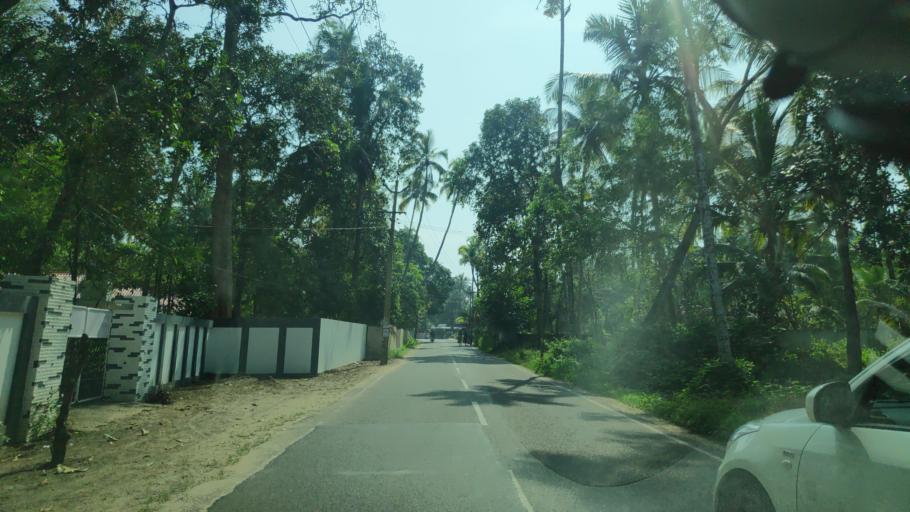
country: IN
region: Kerala
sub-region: Alappuzha
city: Vayalar
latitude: 9.6474
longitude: 76.2992
